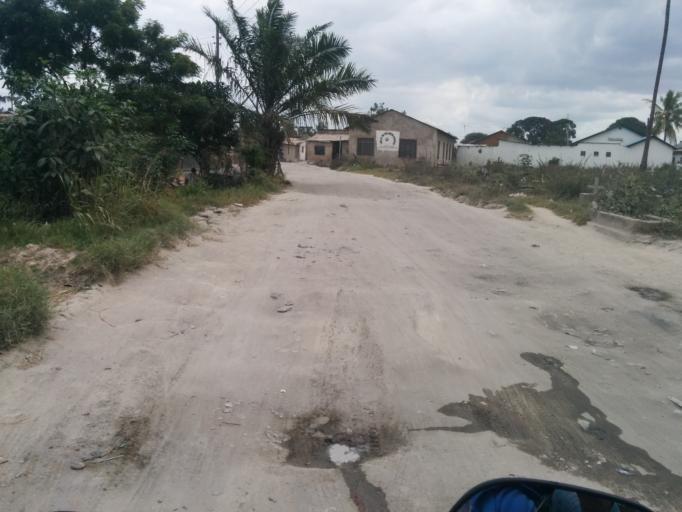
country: TZ
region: Dar es Salaam
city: Dar es Salaam
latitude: -6.8685
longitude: 39.2448
